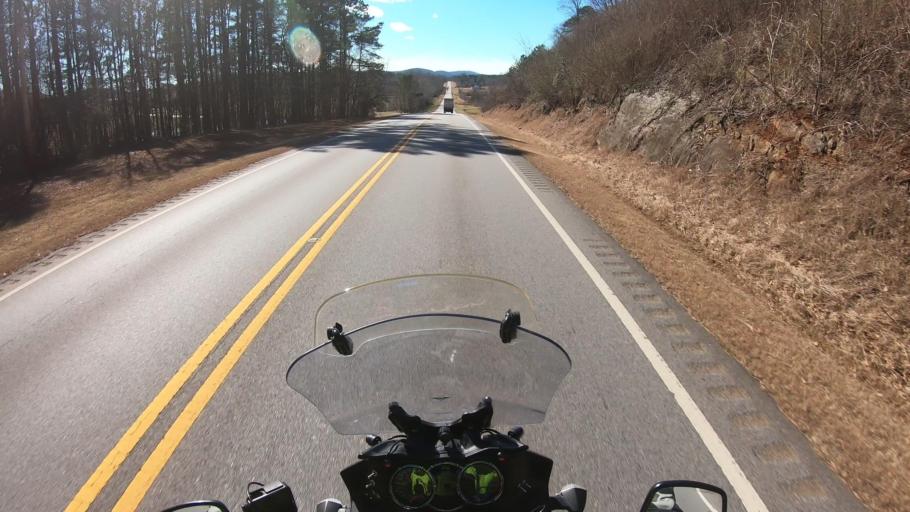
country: US
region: Alabama
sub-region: Calhoun County
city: Choccolocco
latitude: 33.4822
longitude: -85.6866
